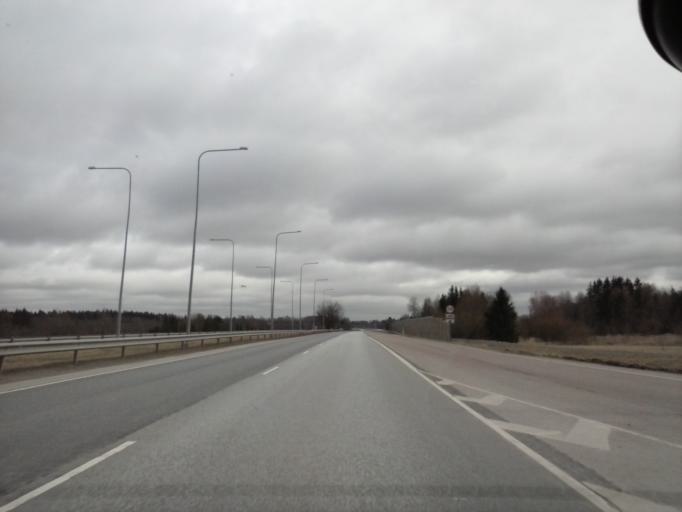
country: EE
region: Harju
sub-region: Rae vald
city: Vaida
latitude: 59.3115
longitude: 24.9363
